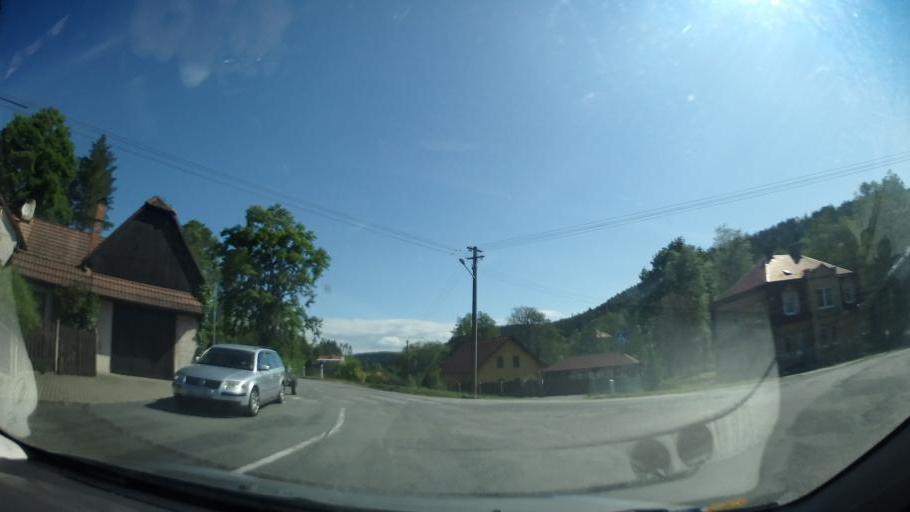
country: CZ
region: South Moravian
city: Velke Opatovice
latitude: 49.6511
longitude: 16.6200
